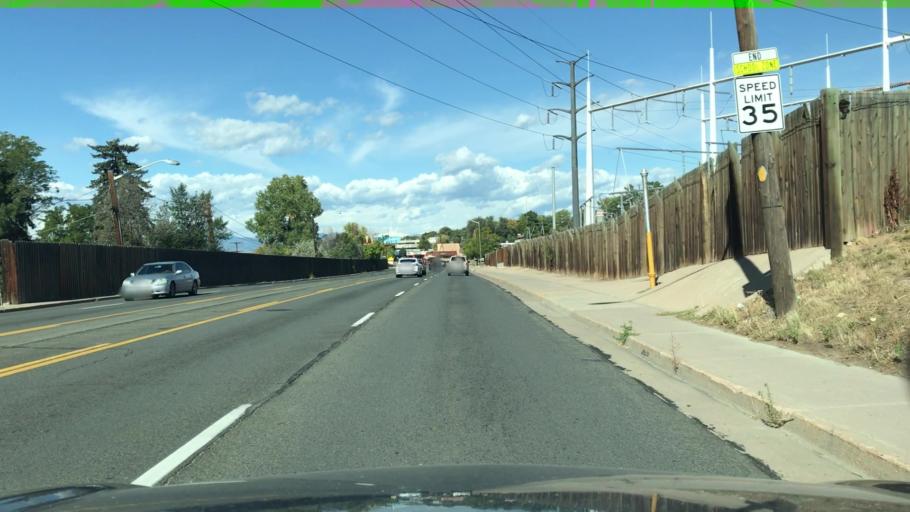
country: US
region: Colorado
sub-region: Arapahoe County
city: Glendale
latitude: 39.7054
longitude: -104.9176
